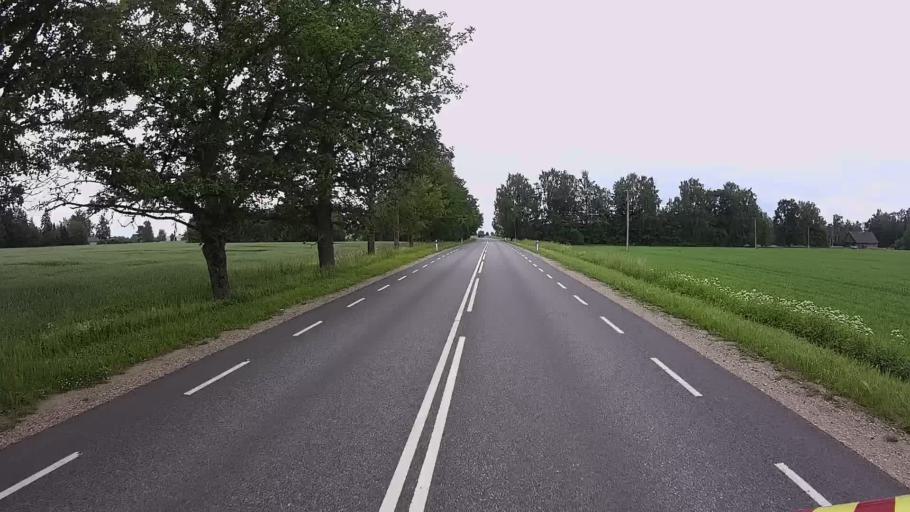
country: EE
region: Viljandimaa
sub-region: Karksi vald
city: Karksi-Nuia
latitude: 58.1350
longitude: 25.5839
